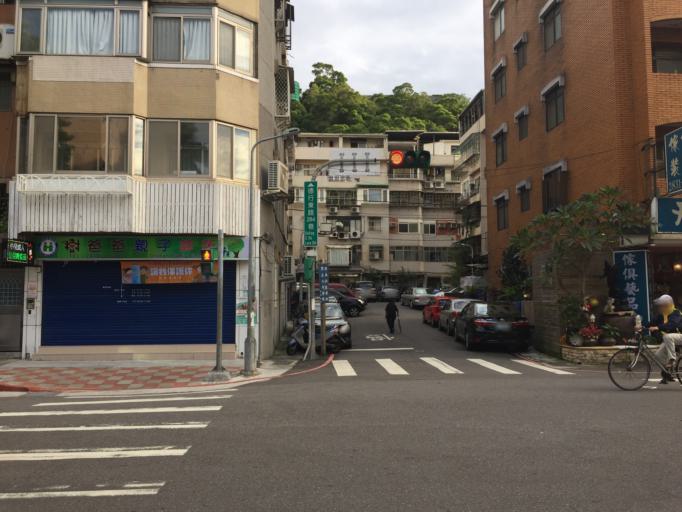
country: TW
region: Taipei
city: Taipei
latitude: 25.1101
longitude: 121.5360
